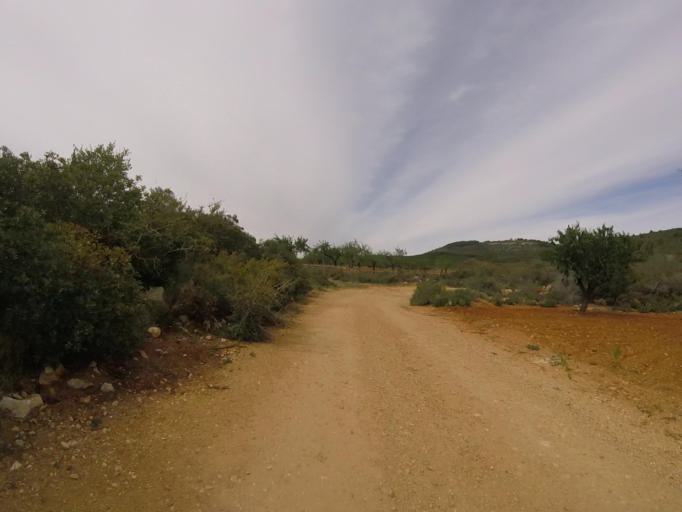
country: ES
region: Valencia
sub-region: Provincia de Castello
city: Cabanes
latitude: 40.1904
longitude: 0.0940
